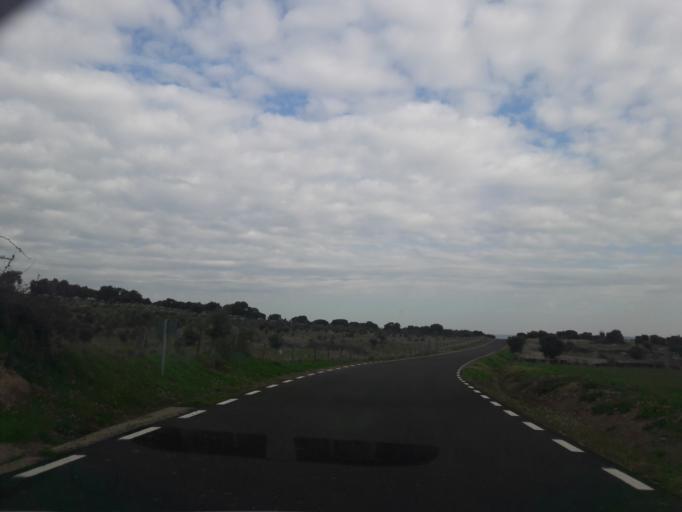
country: ES
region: Castille and Leon
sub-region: Provincia de Salamanca
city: Pastores
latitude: 40.5088
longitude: -6.5285
